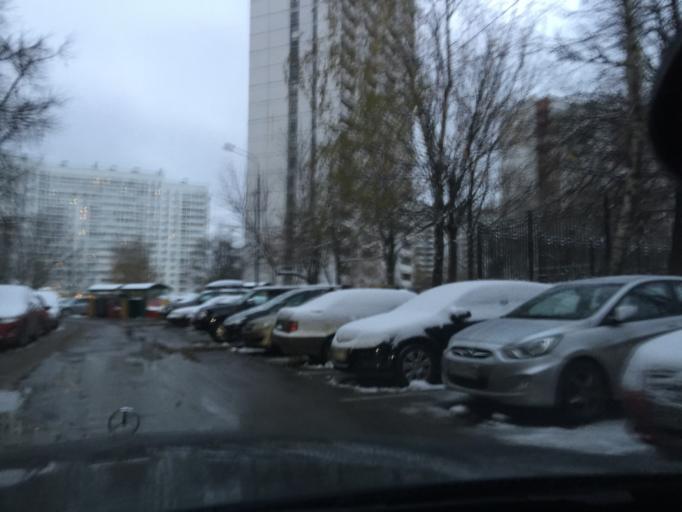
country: RU
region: Moscow
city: Troparevo
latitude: 55.6429
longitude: 37.4770
